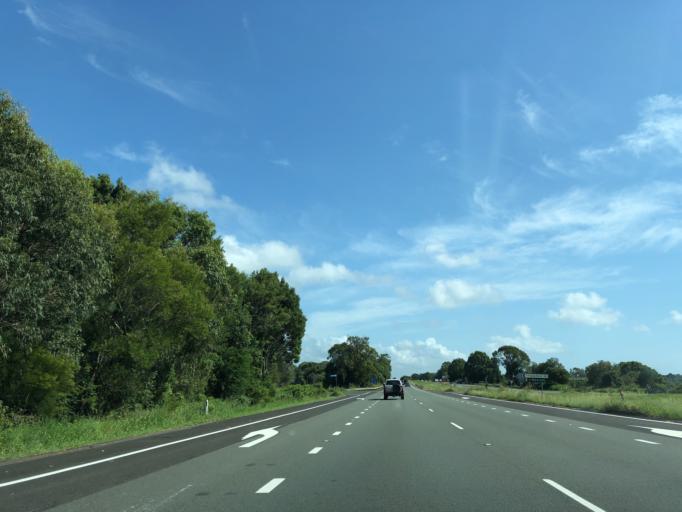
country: AU
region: New South Wales
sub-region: Byron Shire
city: Brunswick Heads
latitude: -28.6092
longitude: 153.5464
